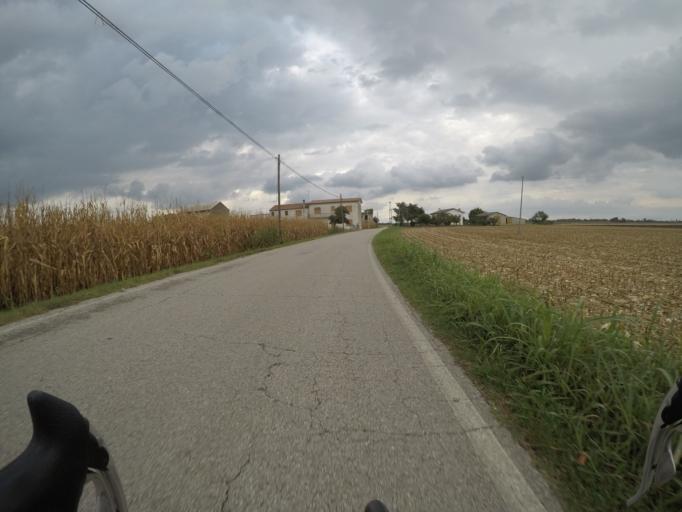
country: IT
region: Veneto
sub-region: Provincia di Rovigo
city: Polesella
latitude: 44.9783
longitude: 11.7246
